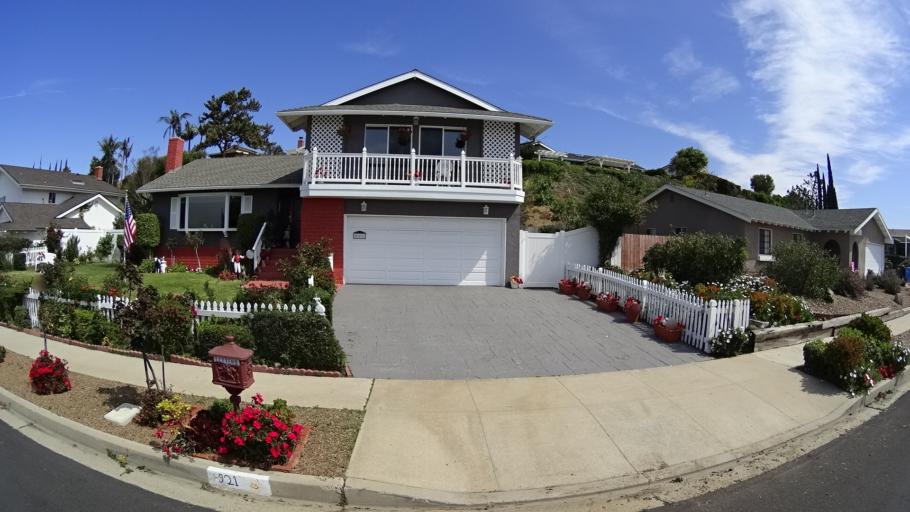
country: US
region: California
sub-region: Ventura County
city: Moorpark
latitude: 34.2317
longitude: -118.8623
